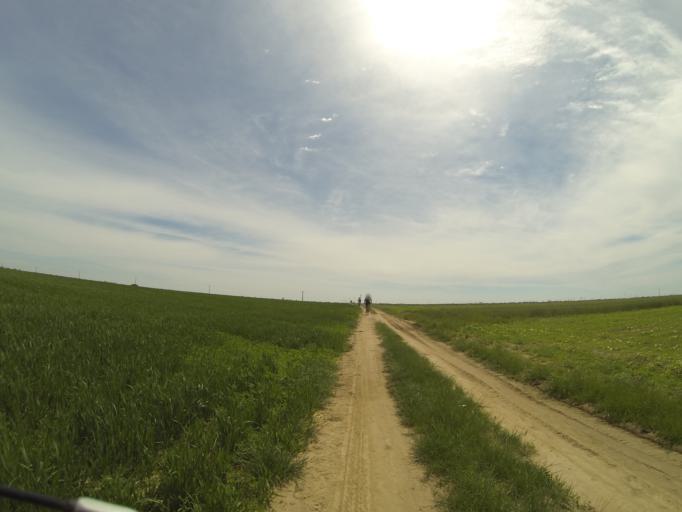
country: RO
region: Dolj
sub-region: Comuna Ghindeni
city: Ghindeni
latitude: 44.2065
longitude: 23.9552
